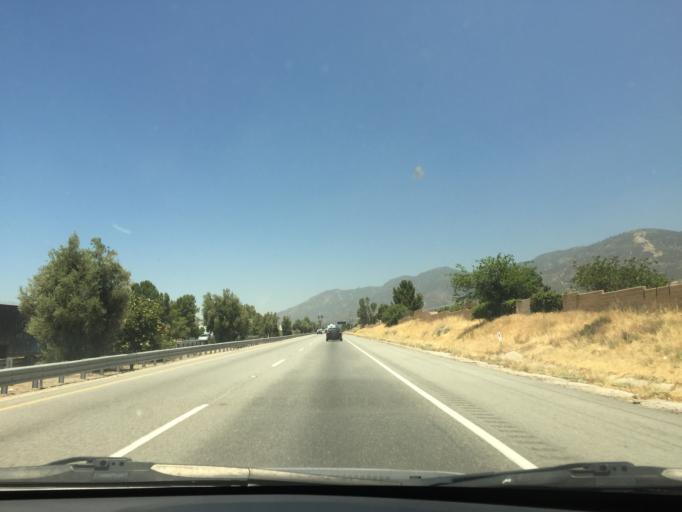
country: US
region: California
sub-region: San Bernardino County
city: Muscoy
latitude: 34.1735
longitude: -117.3410
